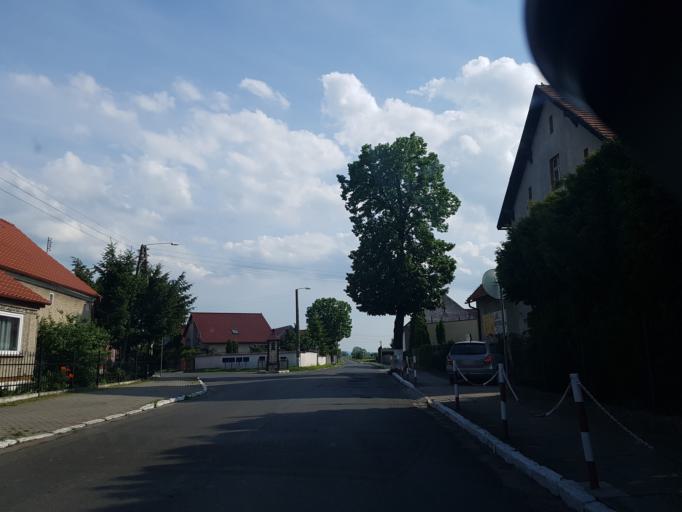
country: PL
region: Lower Silesian Voivodeship
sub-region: Powiat olawski
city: Wierzbno
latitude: 50.8933
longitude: 17.1307
